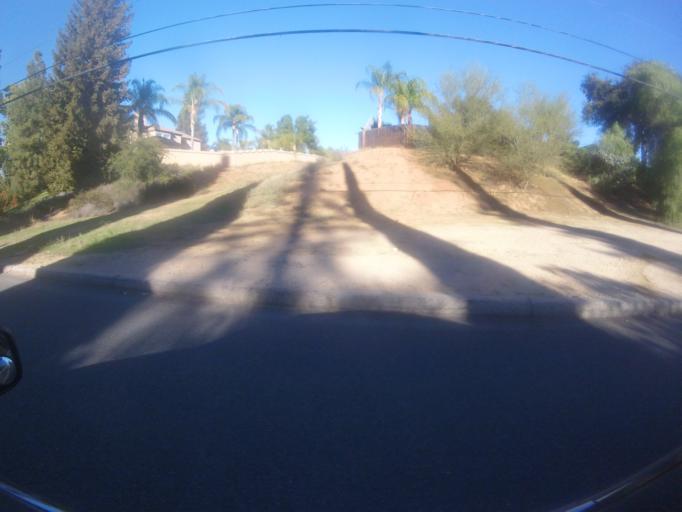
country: US
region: California
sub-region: San Bernardino County
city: Redlands
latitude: 34.0263
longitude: -117.1780
